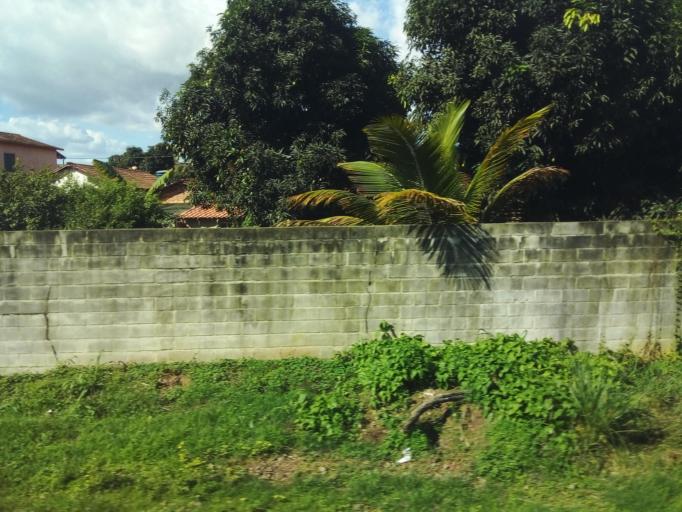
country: BR
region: Minas Gerais
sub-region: Conselheiro Pena
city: Conselheiro Pena
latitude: -18.9795
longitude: -41.6513
